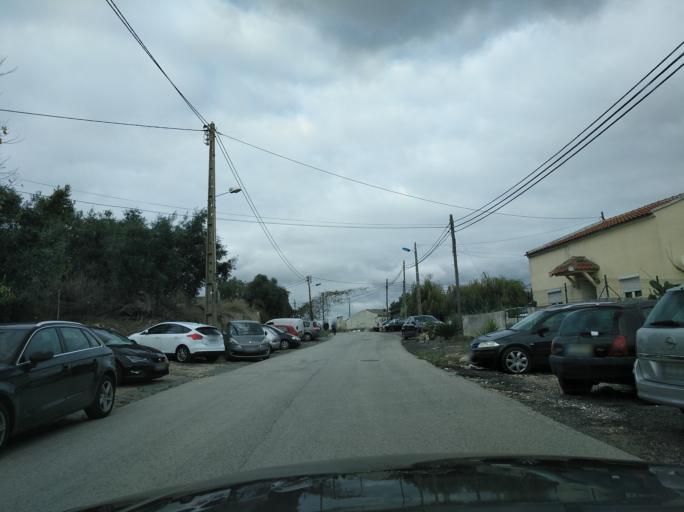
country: PT
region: Lisbon
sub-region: Loures
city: Moscavide
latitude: 38.7613
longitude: -9.1361
